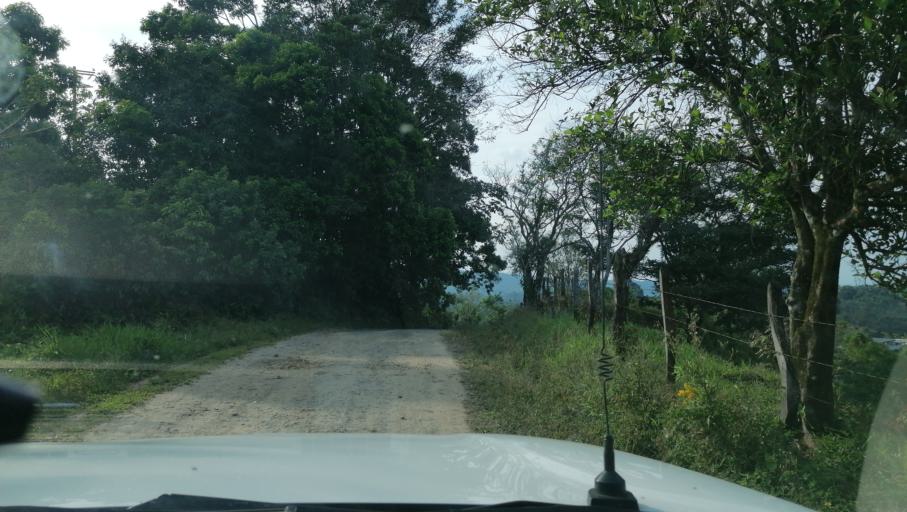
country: MX
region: Chiapas
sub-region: Juarez
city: El Triunfo 1ra. Seccion (Cardona)
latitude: 17.4860
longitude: -93.2377
